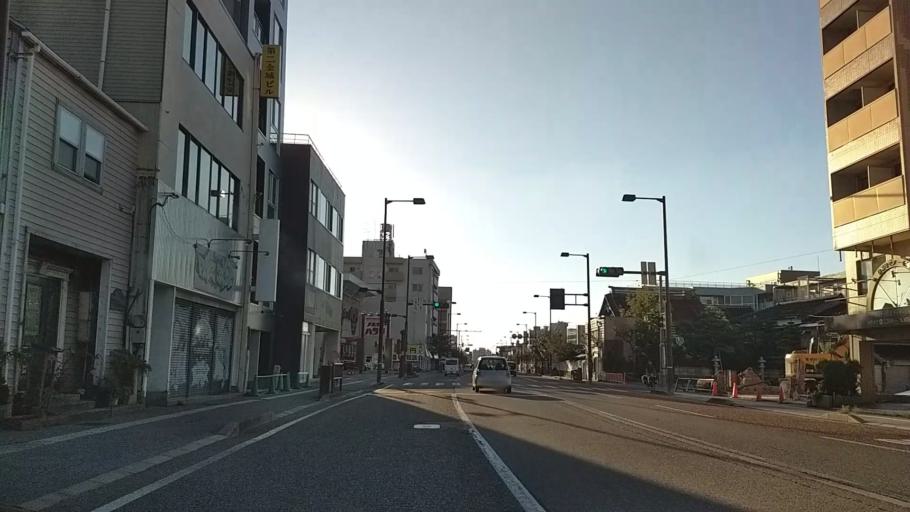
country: JP
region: Ishikawa
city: Nonoichi
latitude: 36.5580
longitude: 136.6462
